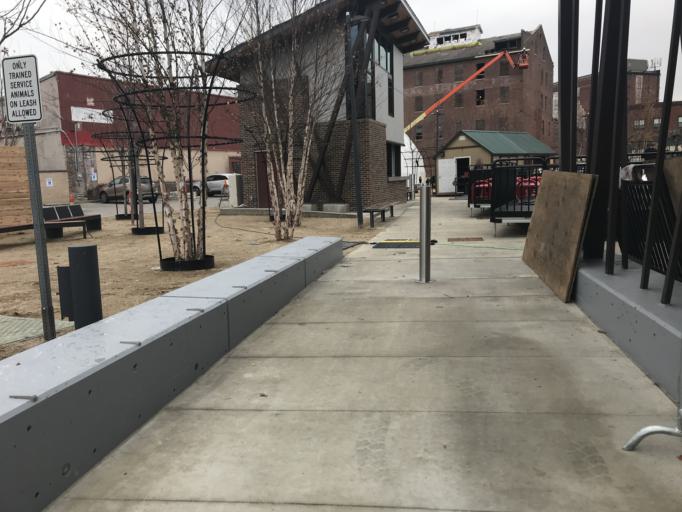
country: US
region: Kentucky
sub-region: Jefferson County
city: Louisville
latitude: 38.2429
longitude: -85.7354
